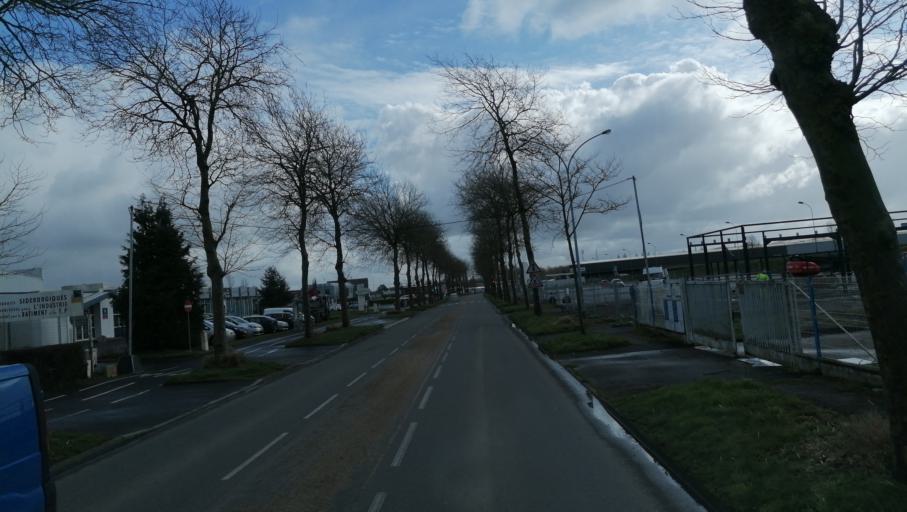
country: FR
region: Brittany
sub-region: Departement des Cotes-d'Armor
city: Saint-Julien
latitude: 48.4687
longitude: -2.7976
